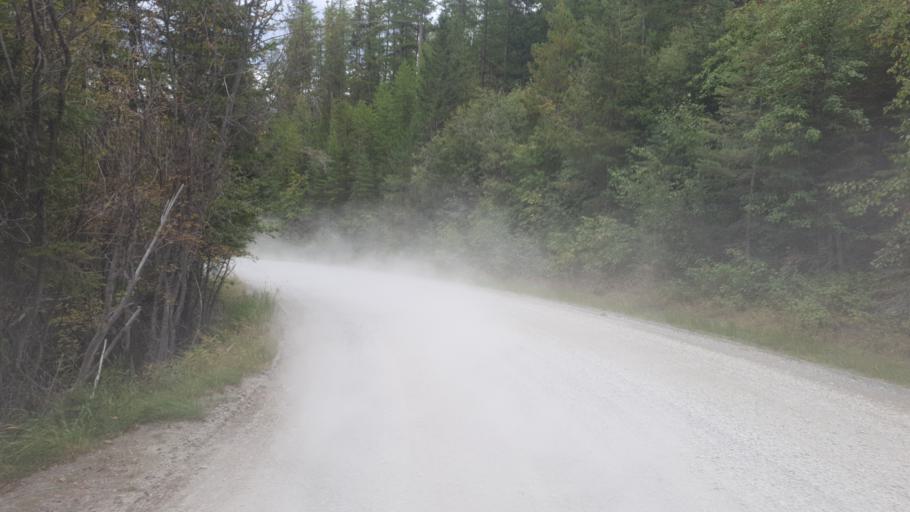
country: US
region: Montana
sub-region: Flathead County
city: Lakeside
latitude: 47.9923
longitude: -114.3249
